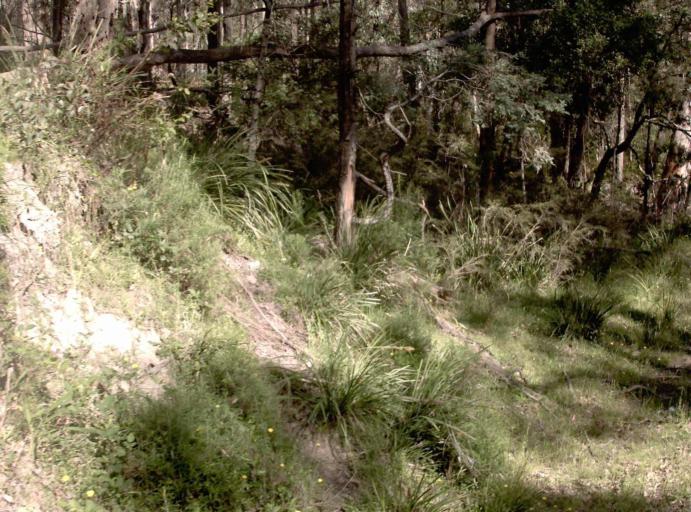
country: AU
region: New South Wales
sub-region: Bombala
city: Bombala
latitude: -37.3588
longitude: 148.6836
